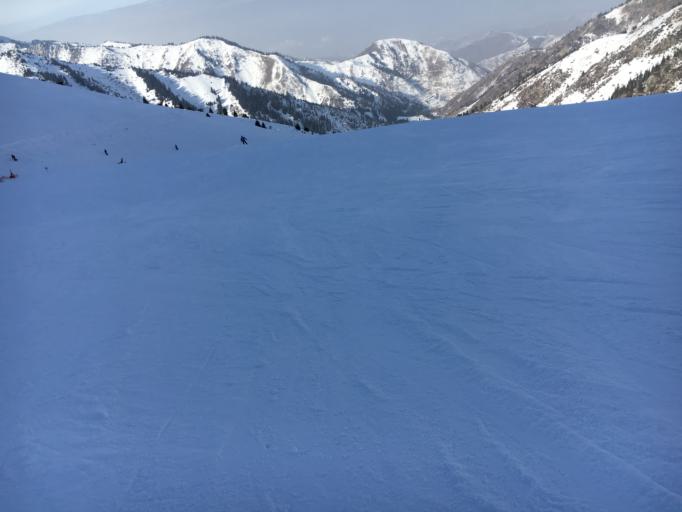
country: KZ
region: Almaty Qalasy
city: Almaty
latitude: 43.1187
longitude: 77.0984
